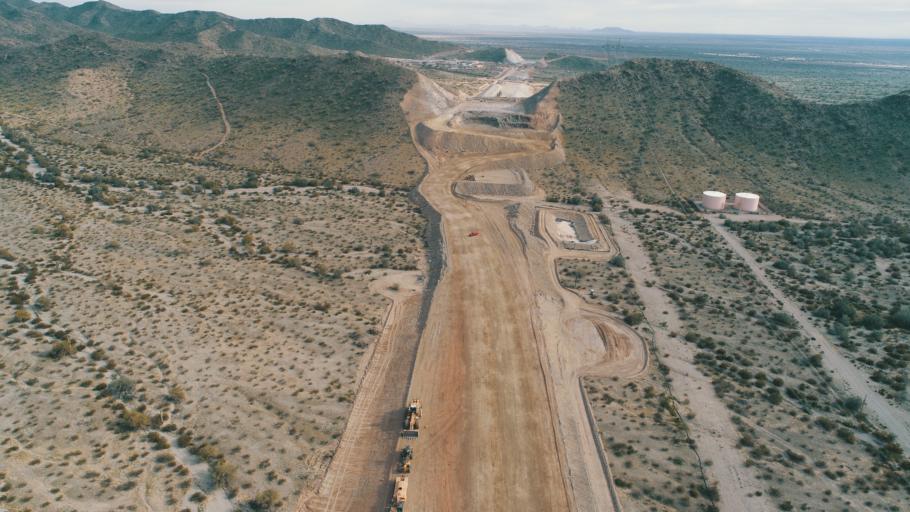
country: US
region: Arizona
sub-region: Maricopa County
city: Laveen
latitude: 33.3096
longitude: -112.1513
